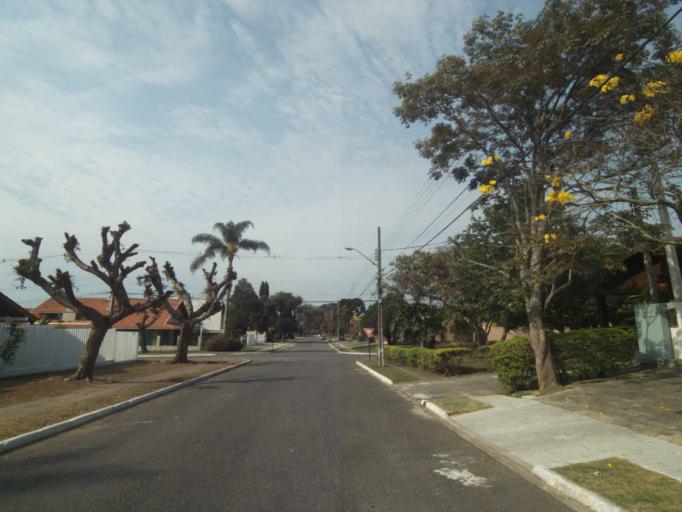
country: BR
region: Parana
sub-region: Pinhais
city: Pinhais
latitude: -25.4799
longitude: -49.2069
